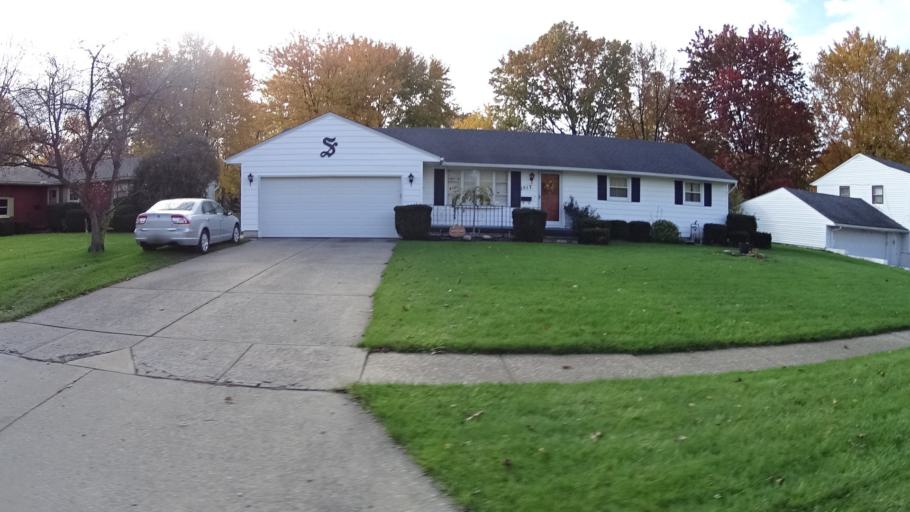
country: US
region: Ohio
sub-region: Lorain County
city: Lorain
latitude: 41.4323
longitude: -82.1918
